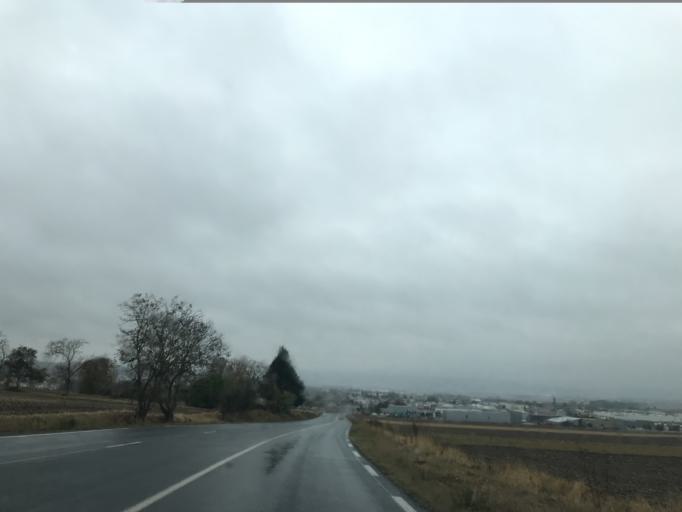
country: FR
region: Auvergne
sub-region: Departement du Puy-de-Dome
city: Dallet
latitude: 45.7727
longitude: 3.2182
